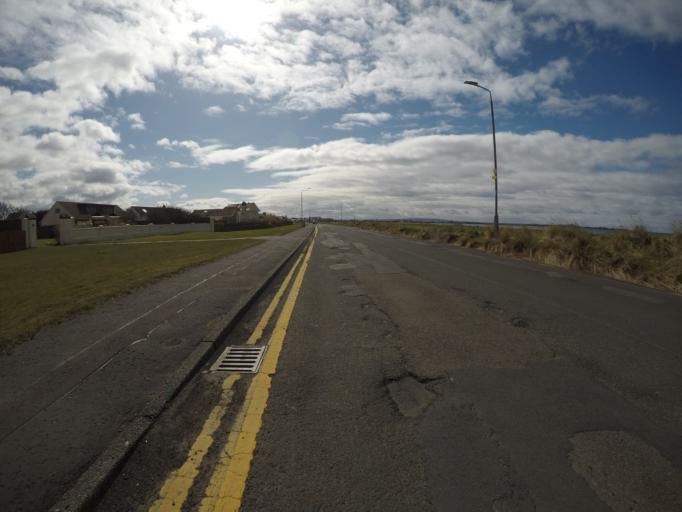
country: GB
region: Scotland
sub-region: South Ayrshire
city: Troon
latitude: 55.5644
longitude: -4.6580
